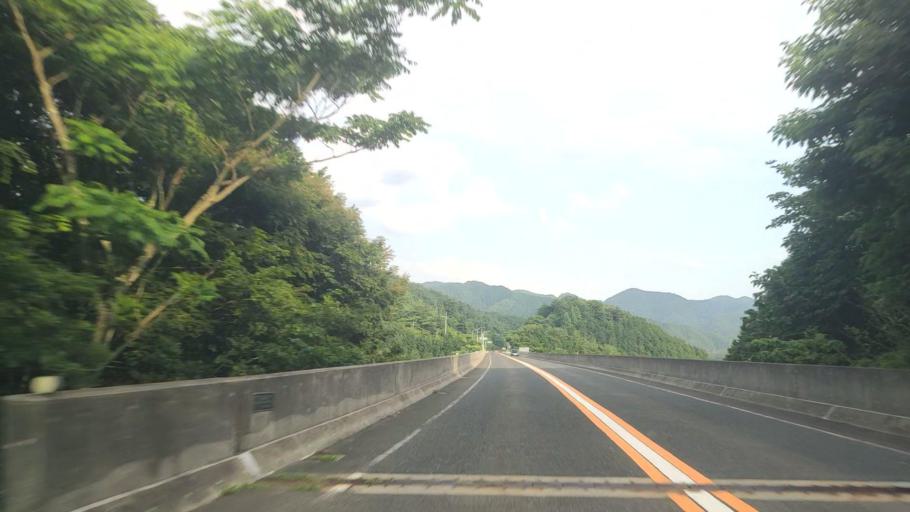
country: JP
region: Tottori
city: Kurayoshi
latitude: 35.3413
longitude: 133.7499
